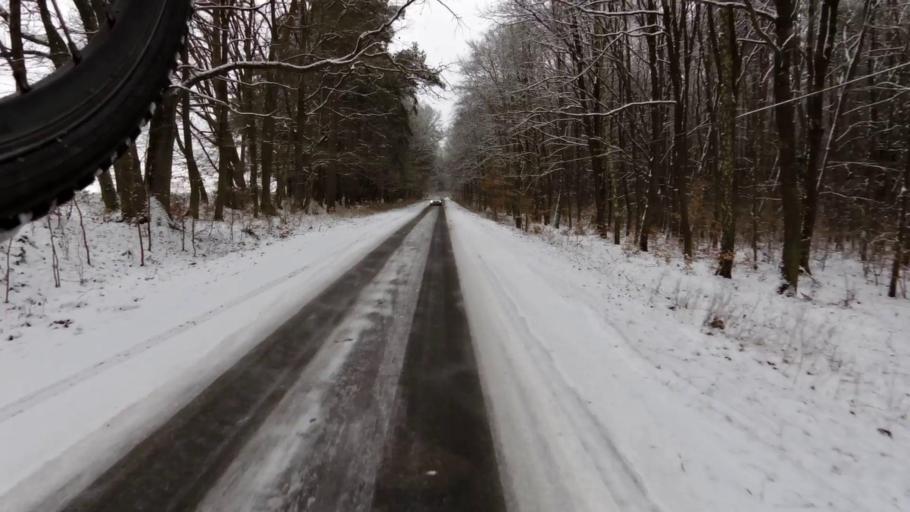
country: PL
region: West Pomeranian Voivodeship
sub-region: Powiat swidwinski
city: Rabino
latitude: 53.8902
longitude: 15.9406
